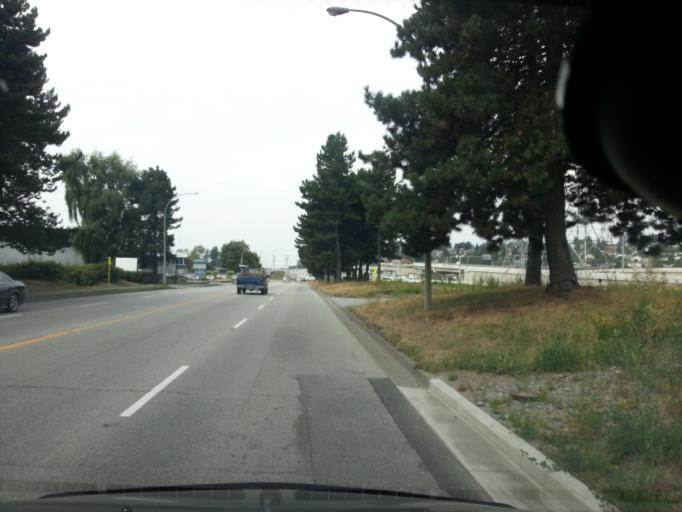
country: CA
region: British Columbia
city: Port Moody
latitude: 49.2266
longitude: -122.8251
